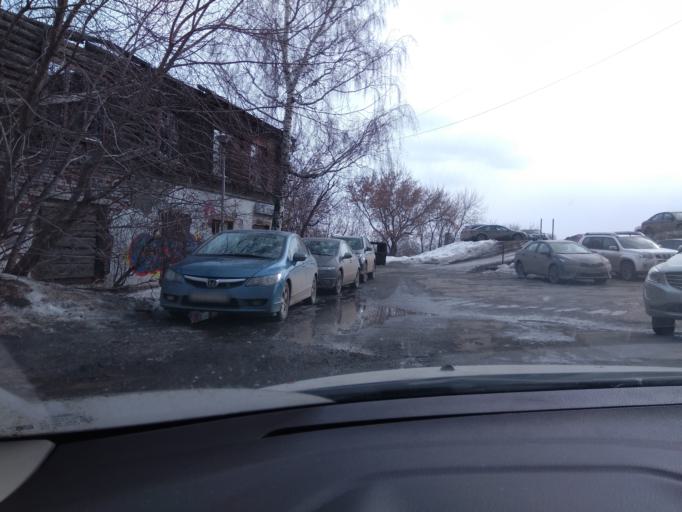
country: RU
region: Sverdlovsk
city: Yekaterinburg
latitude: 56.8268
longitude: 60.6323
